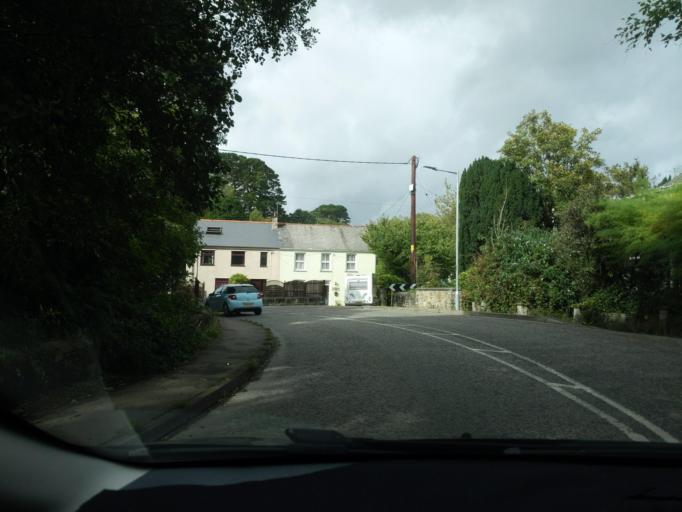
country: GB
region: England
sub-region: Cornwall
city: Par
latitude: 50.3587
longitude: -4.7054
